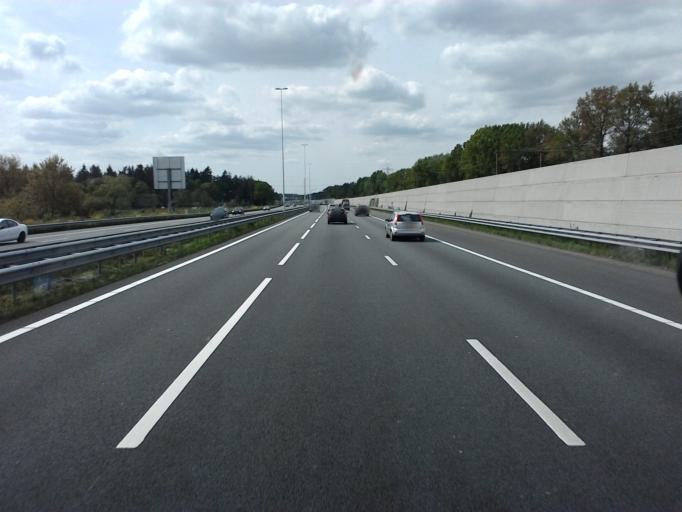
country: NL
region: Utrecht
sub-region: Gemeente Utrechtse Heuvelrug
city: Maarn
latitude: 52.0596
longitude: 5.3874
